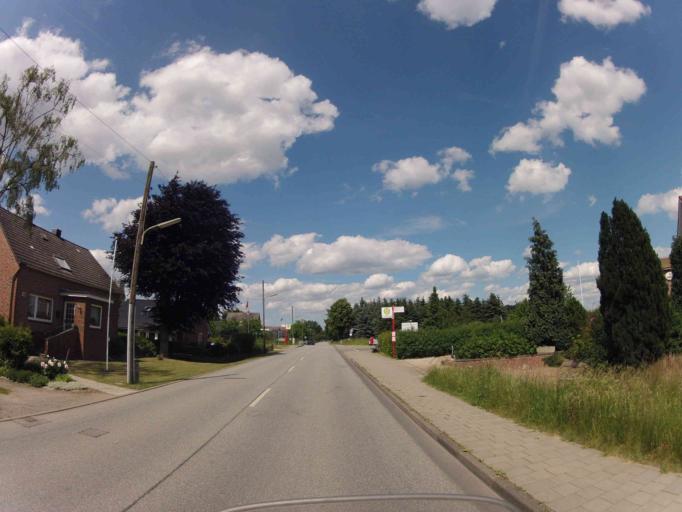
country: DE
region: Lower Saxony
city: Winsen
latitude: 53.4108
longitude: 10.1907
